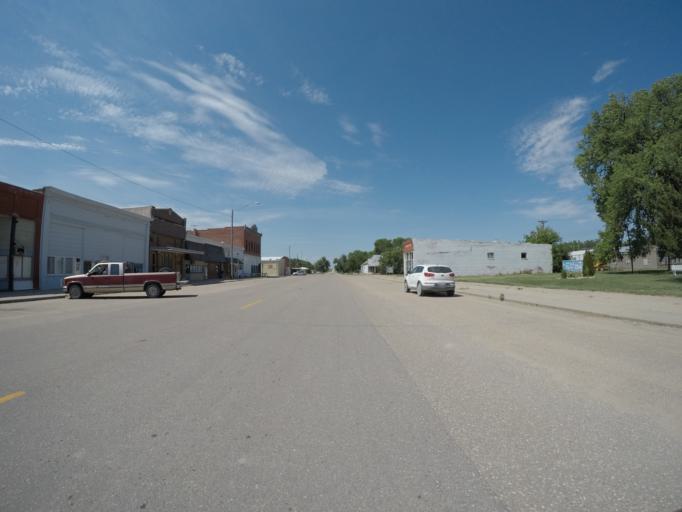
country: US
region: Kansas
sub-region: Jewell County
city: Mankato
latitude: 39.8701
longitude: -98.3060
